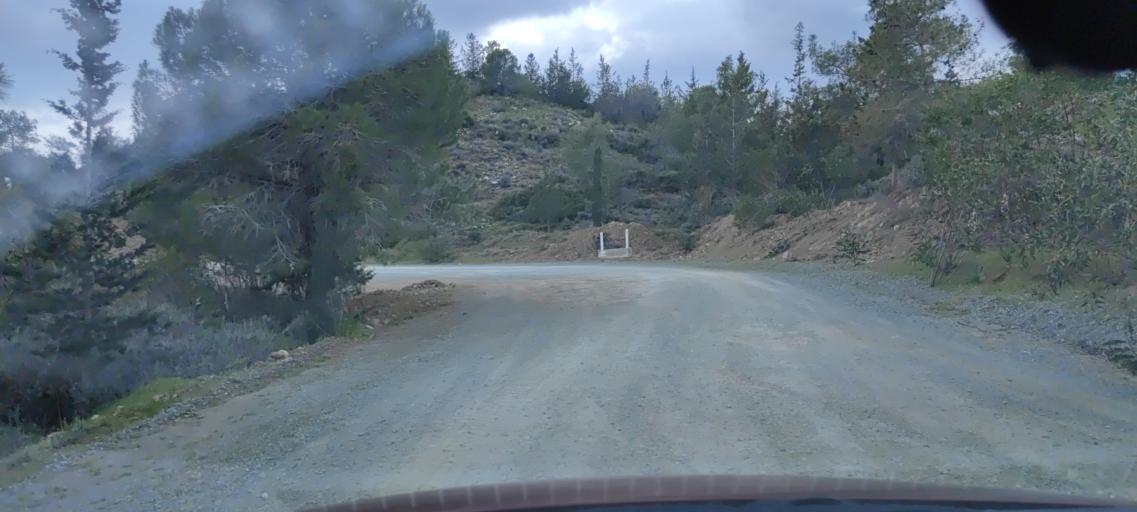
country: CY
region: Larnaka
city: Kornos
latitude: 34.9107
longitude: 33.4007
